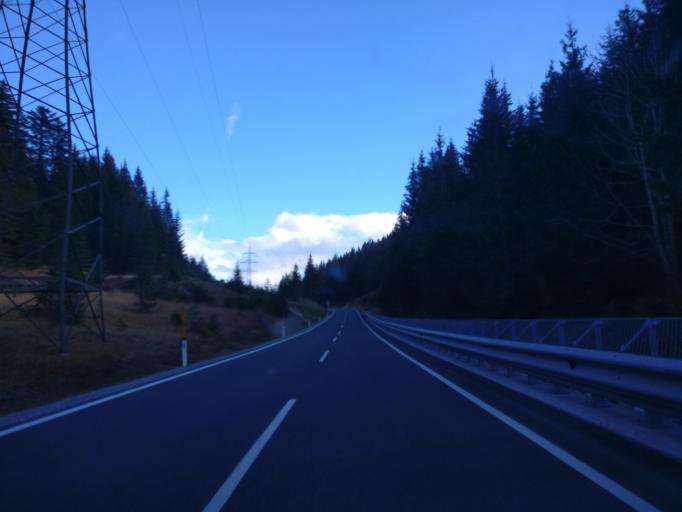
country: AT
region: Salzburg
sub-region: Politischer Bezirk Zell am See
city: Dienten am Hochkonig
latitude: 47.3987
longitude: 12.9970
